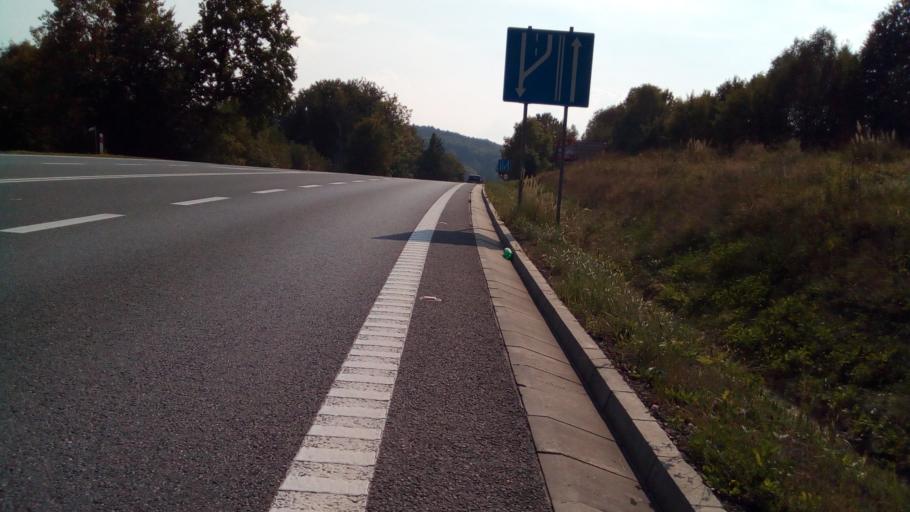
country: PL
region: Subcarpathian Voivodeship
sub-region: Powiat strzyzowski
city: Jawornik
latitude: 49.8373
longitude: 21.8881
